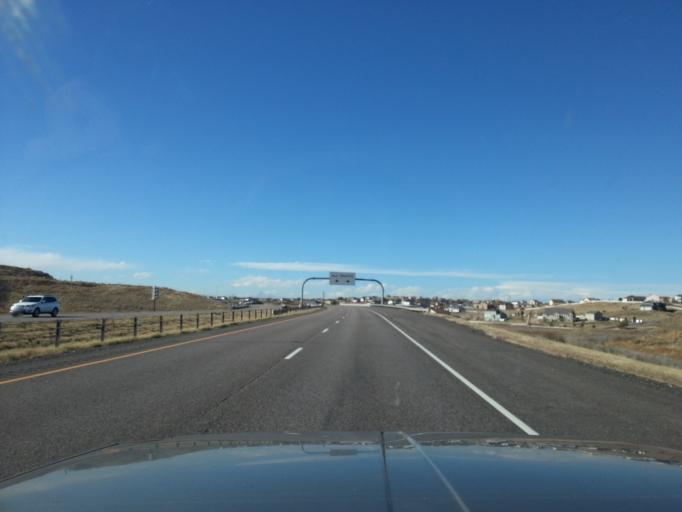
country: US
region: Colorado
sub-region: Adams County
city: Todd Creek
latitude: 39.9506
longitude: -104.8641
